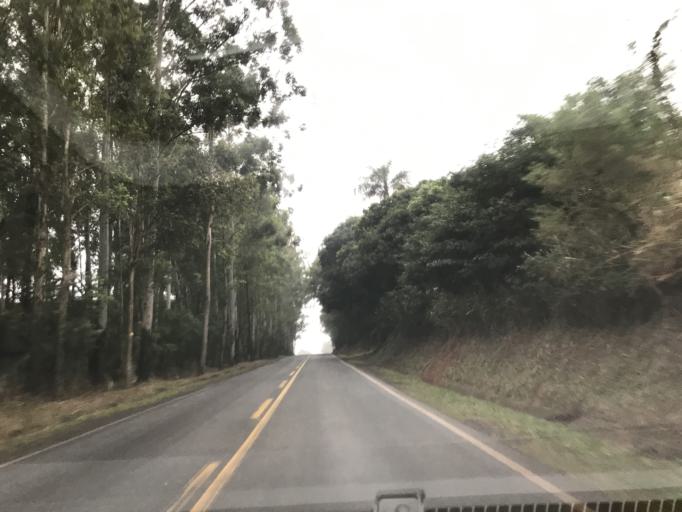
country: PY
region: Canindeyu
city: Salto del Guaira
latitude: -24.1187
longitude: -54.1171
